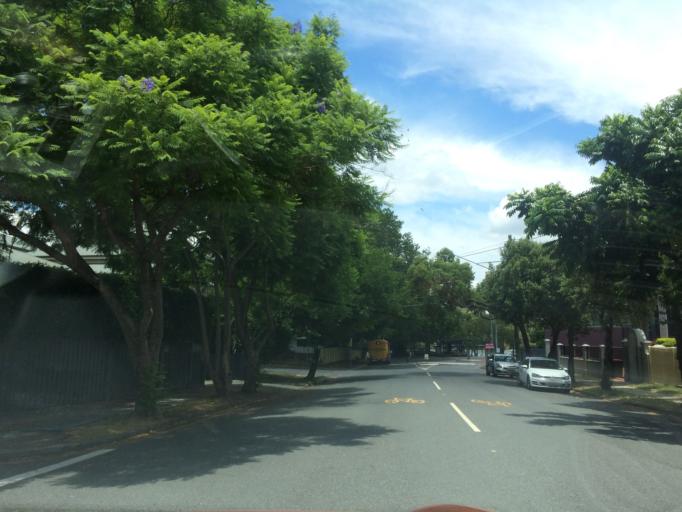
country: AU
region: Queensland
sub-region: Brisbane
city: Toowong
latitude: -27.4887
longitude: 153.0037
